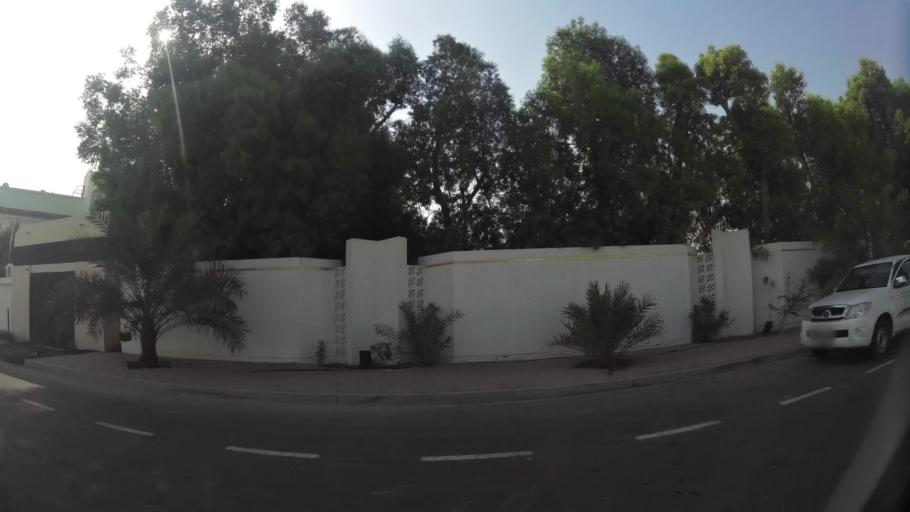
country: AE
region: Ash Shariqah
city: Sharjah
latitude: 25.3134
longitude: 55.3457
